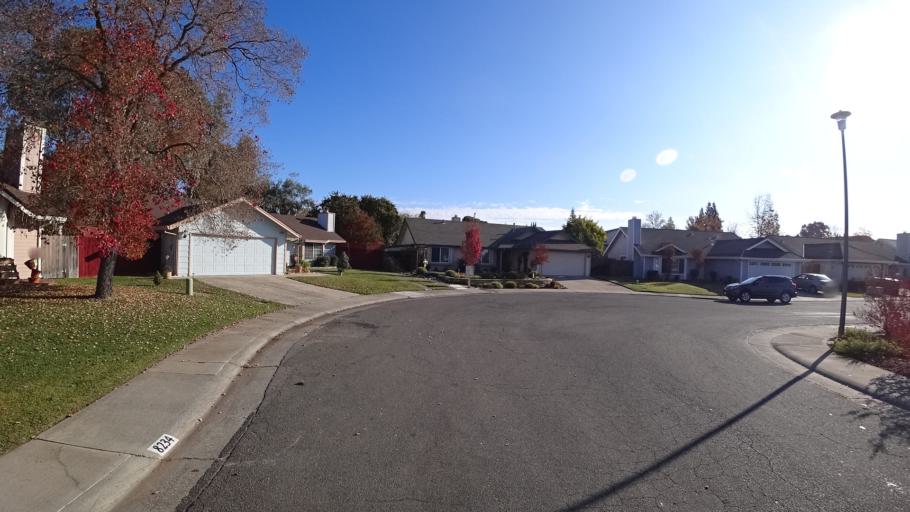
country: US
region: California
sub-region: Sacramento County
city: Citrus Heights
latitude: 38.7166
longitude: -121.2632
